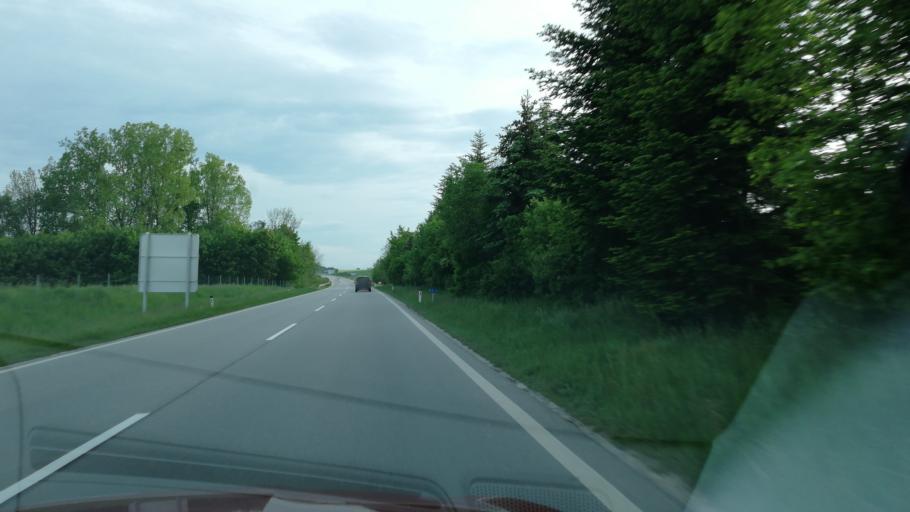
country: AT
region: Upper Austria
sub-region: Wels-Land
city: Steinhaus
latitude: 48.1212
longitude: 14.0467
